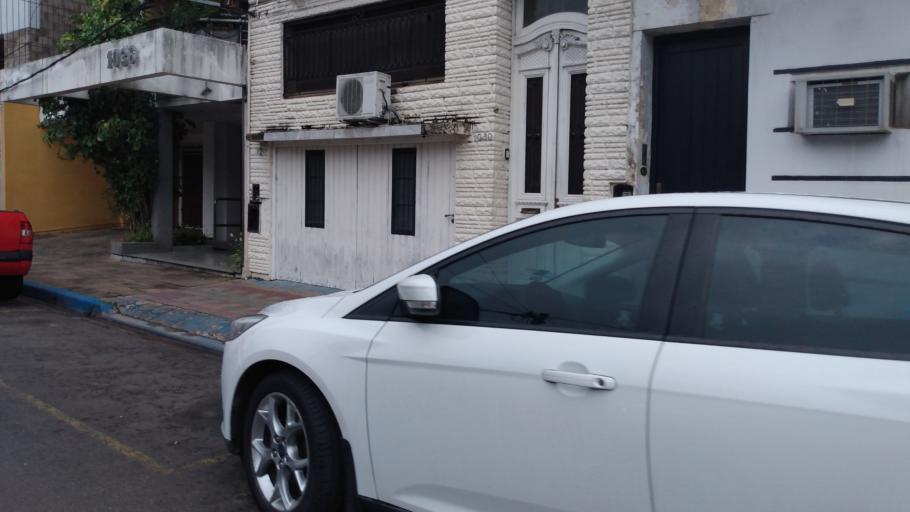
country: AR
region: Corrientes
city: Corrientes
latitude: -27.4694
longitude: -58.8320
